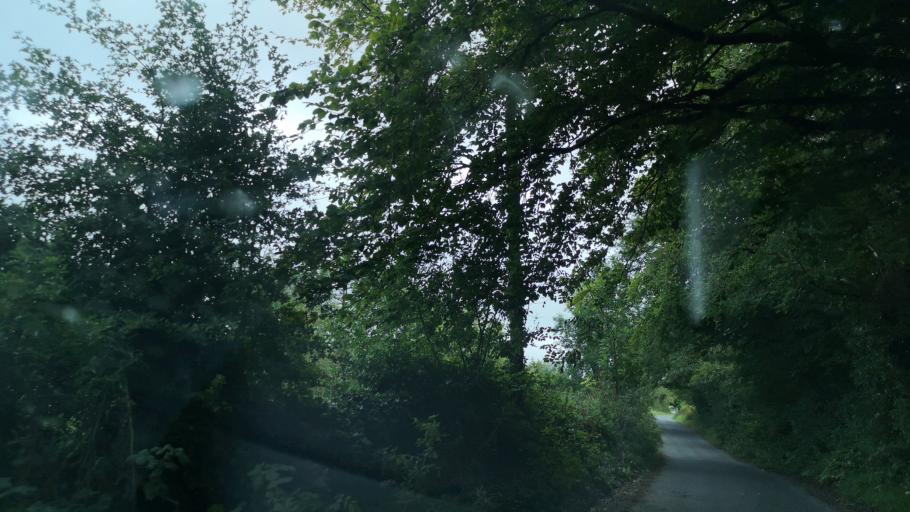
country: IE
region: Connaught
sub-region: County Galway
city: Loughrea
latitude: 53.3015
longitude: -8.6018
